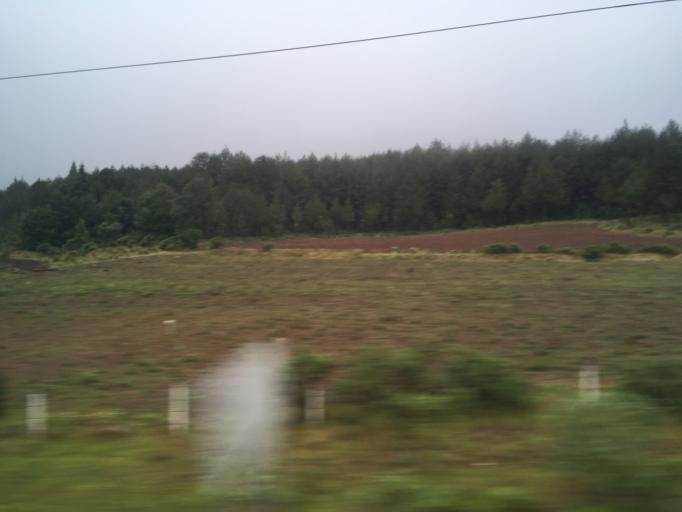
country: MX
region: Puebla
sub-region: Chignahuapan
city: San Antonio Matlahuacales
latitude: 19.7267
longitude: -98.1478
